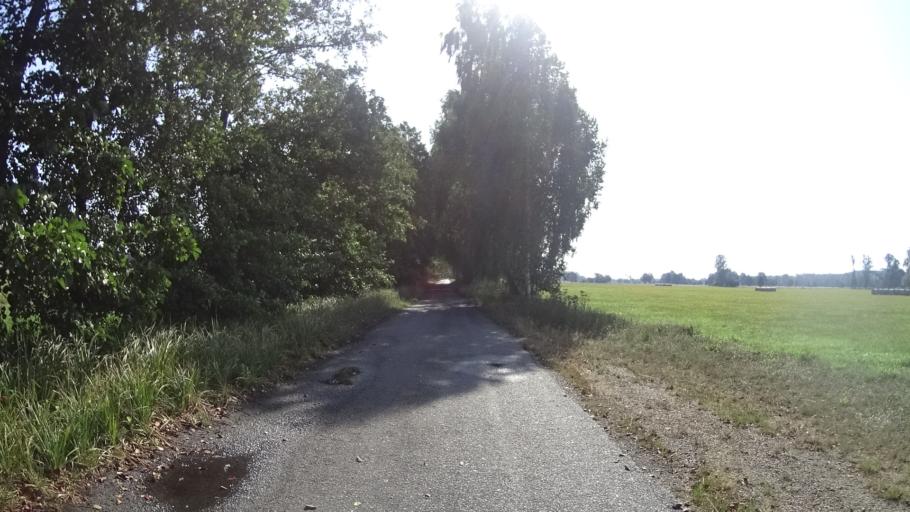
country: DE
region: Brandenburg
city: Straupitz
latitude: 51.9000
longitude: 14.0922
